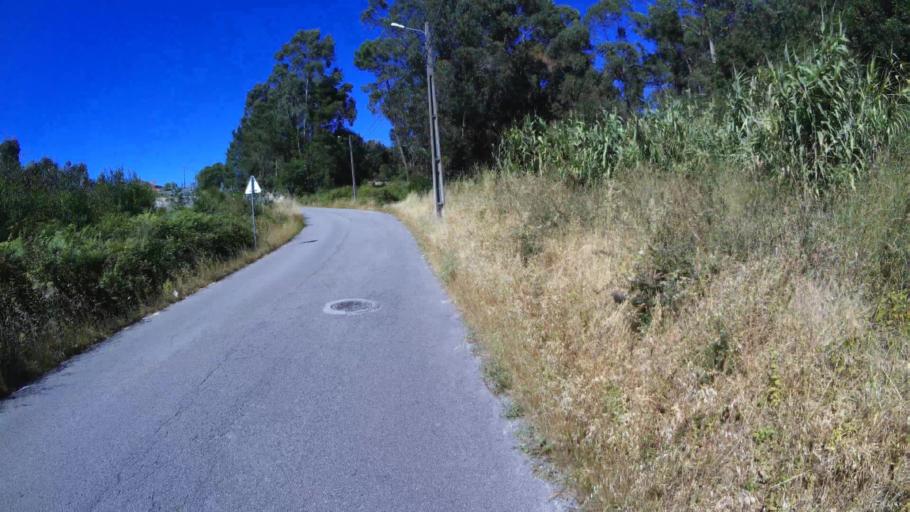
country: PT
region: Aveiro
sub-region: Aveiro
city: Aveiro
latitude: 40.6643
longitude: -8.6198
